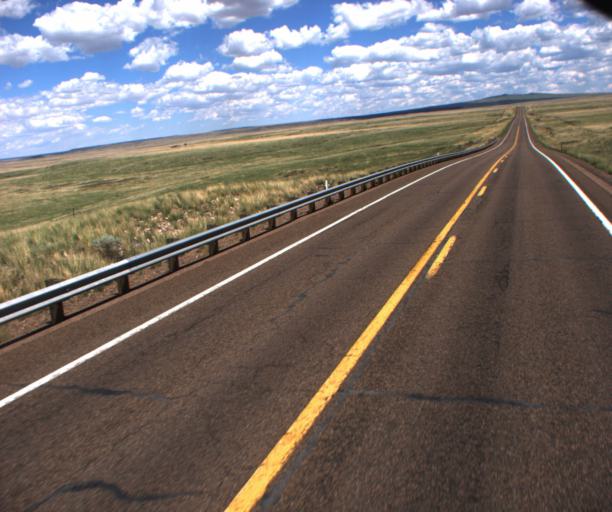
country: US
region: Arizona
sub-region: Apache County
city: Springerville
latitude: 34.1956
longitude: -109.3773
